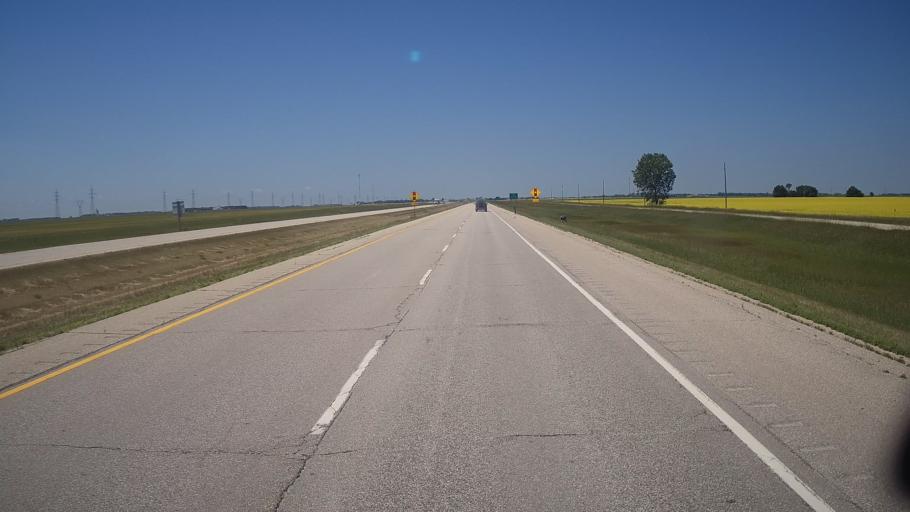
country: CA
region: Manitoba
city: Stonewall
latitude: 49.9900
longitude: -97.2792
